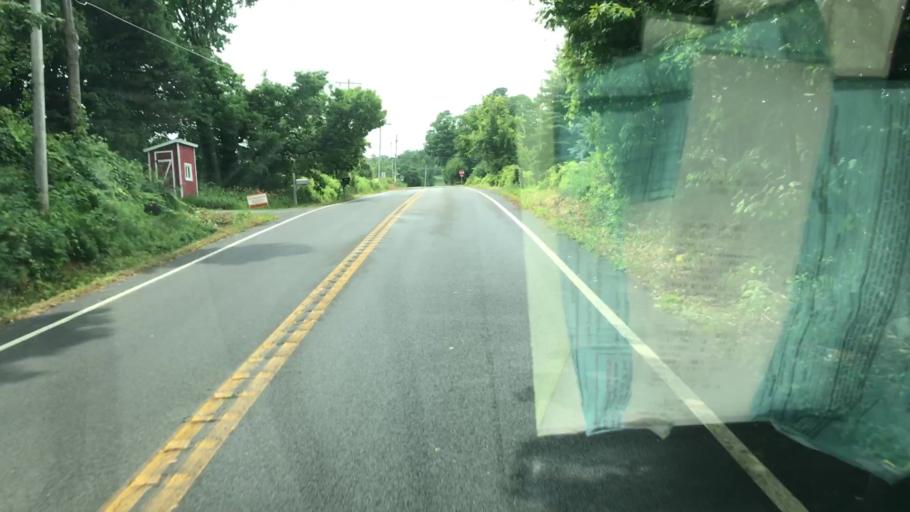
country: US
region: New York
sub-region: Onondaga County
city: Manlius
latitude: 42.9773
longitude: -75.9879
